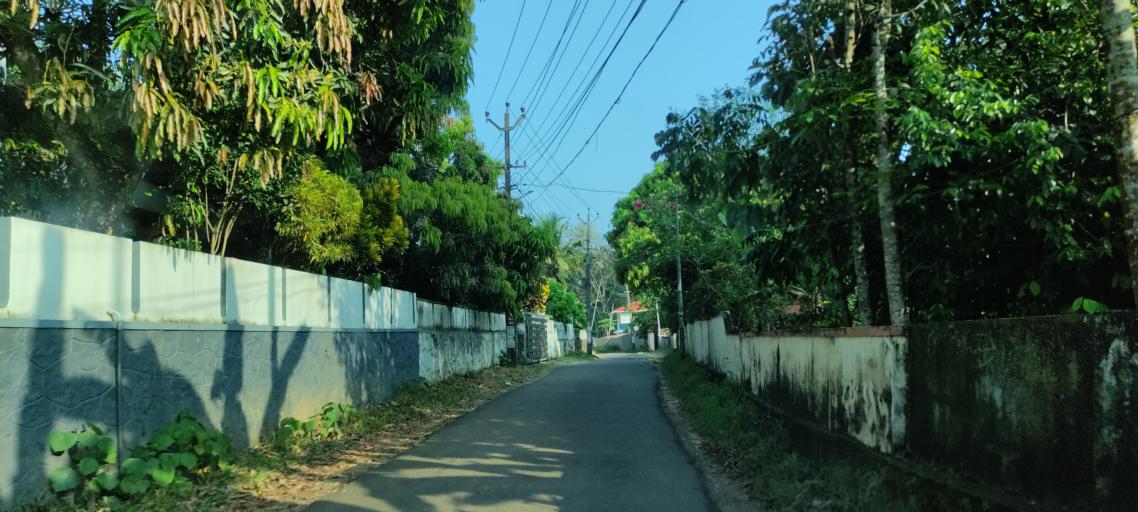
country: IN
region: Kerala
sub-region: Pattanamtitta
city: Adur
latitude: 9.1566
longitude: 76.7428
